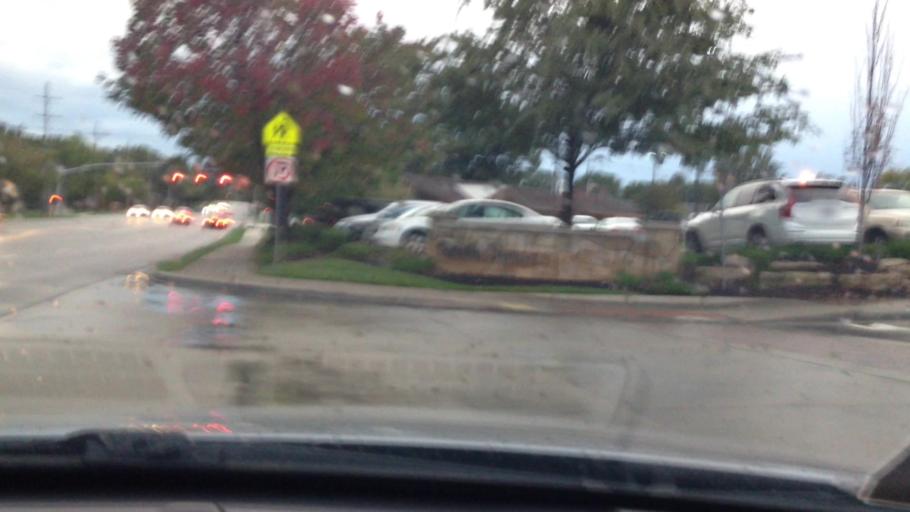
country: US
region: Kansas
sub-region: Johnson County
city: Prairie Village
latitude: 38.9800
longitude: -94.6305
